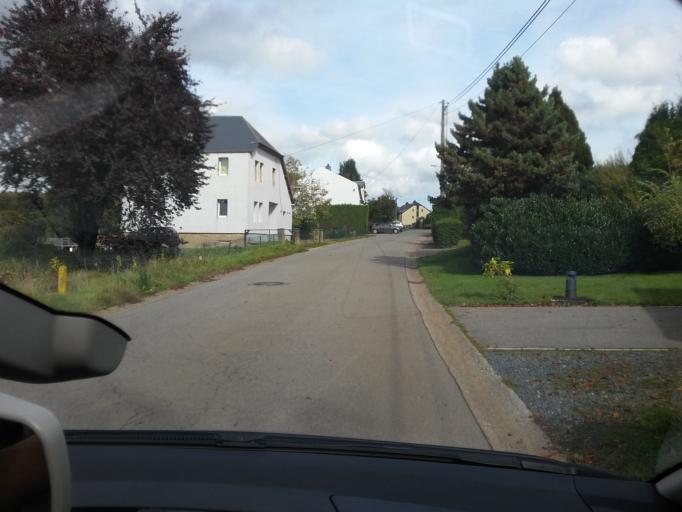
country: BE
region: Wallonia
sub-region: Province du Luxembourg
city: Arlon
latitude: 49.7047
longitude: 5.8011
